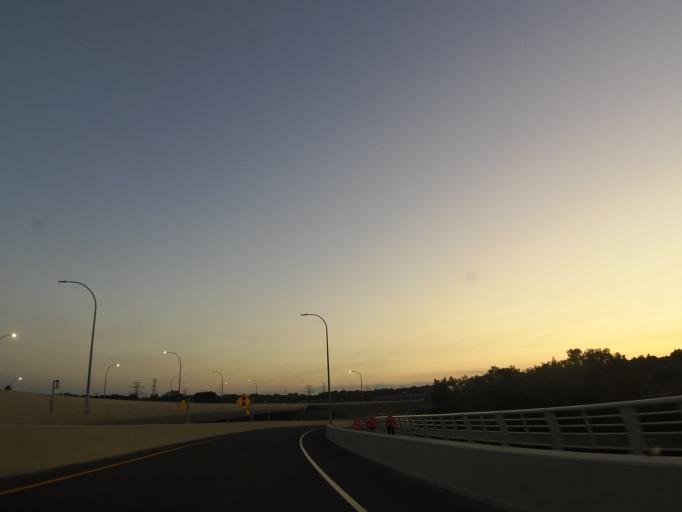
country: US
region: Minnesota
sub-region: Washington County
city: Oak Park Heights
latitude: 45.0374
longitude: -92.7902
